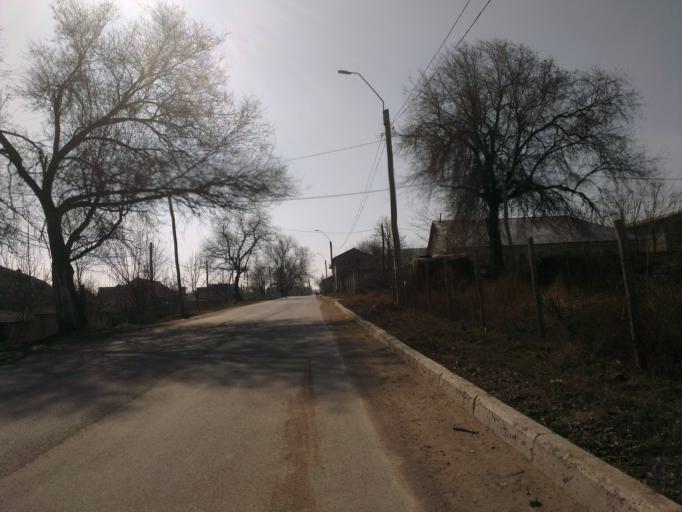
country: MD
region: Chisinau
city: Ciorescu
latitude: 47.1260
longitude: 28.8848
